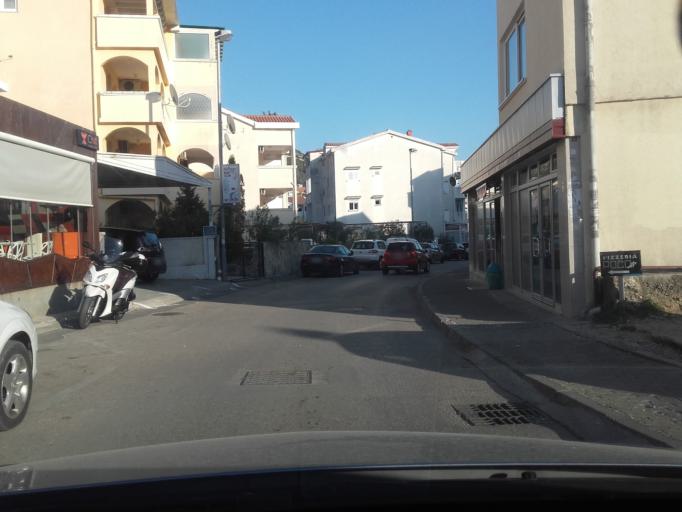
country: ME
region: Budva
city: Budva
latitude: 42.2920
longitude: 18.8464
